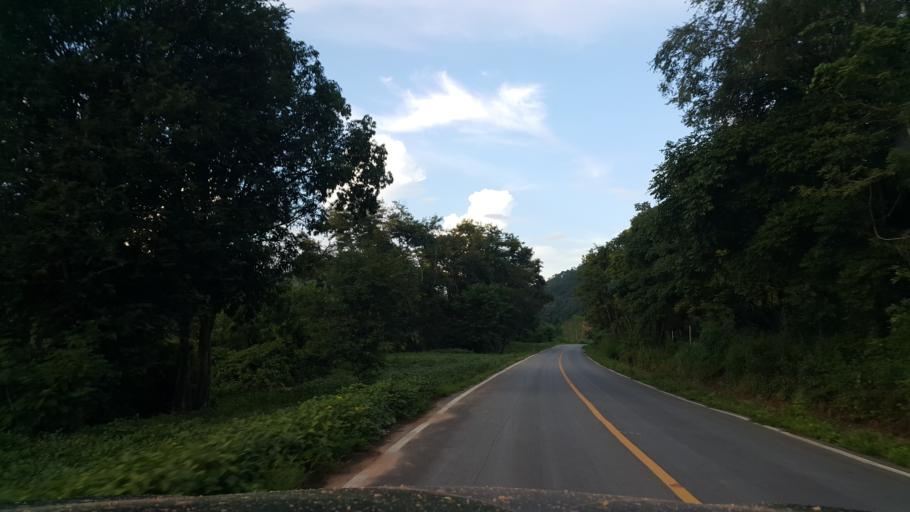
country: TH
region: Mae Hong Son
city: Mae Hi
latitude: 19.2342
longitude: 98.4457
